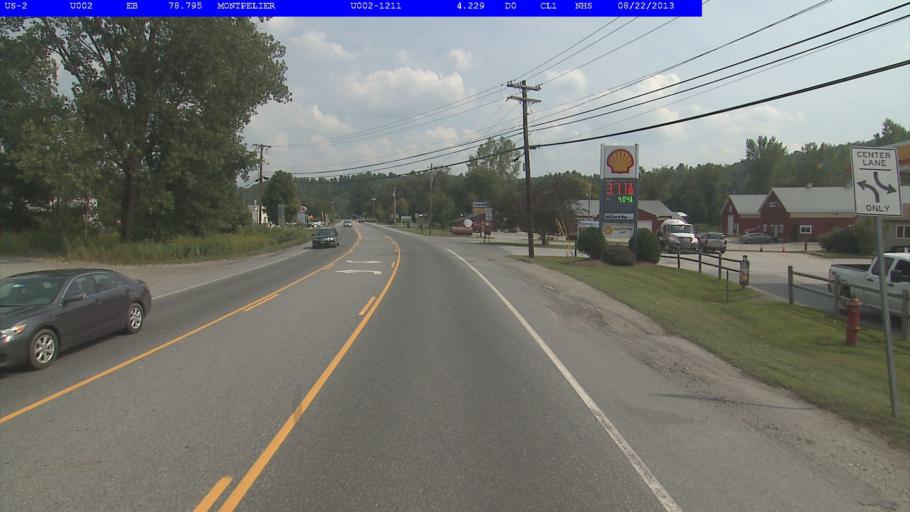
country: US
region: Vermont
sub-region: Washington County
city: Montpelier
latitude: 44.2432
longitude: -72.5462
